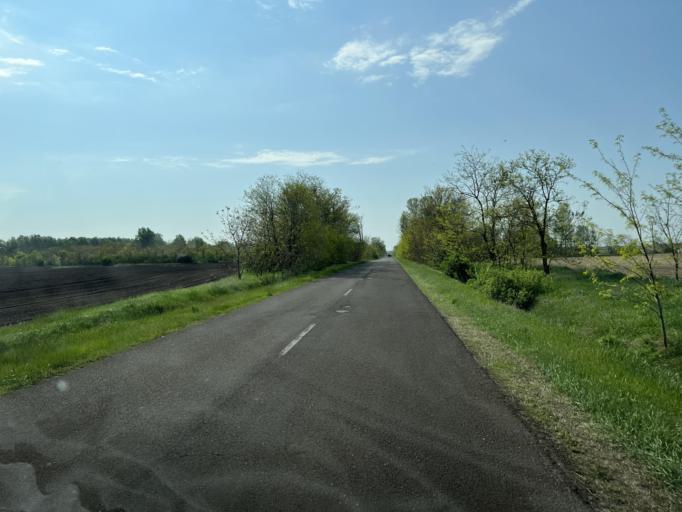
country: HU
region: Pest
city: Jaszkarajeno
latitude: 47.0227
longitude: 20.0392
